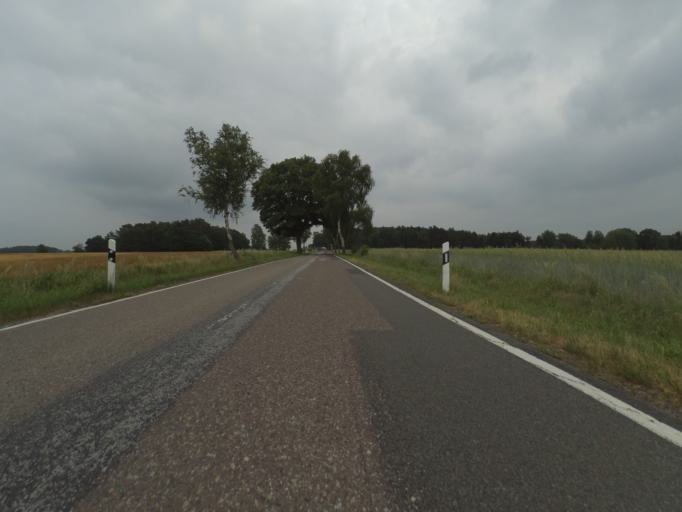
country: DE
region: Mecklenburg-Vorpommern
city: Siggelkow
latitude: 53.3765
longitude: 11.9876
